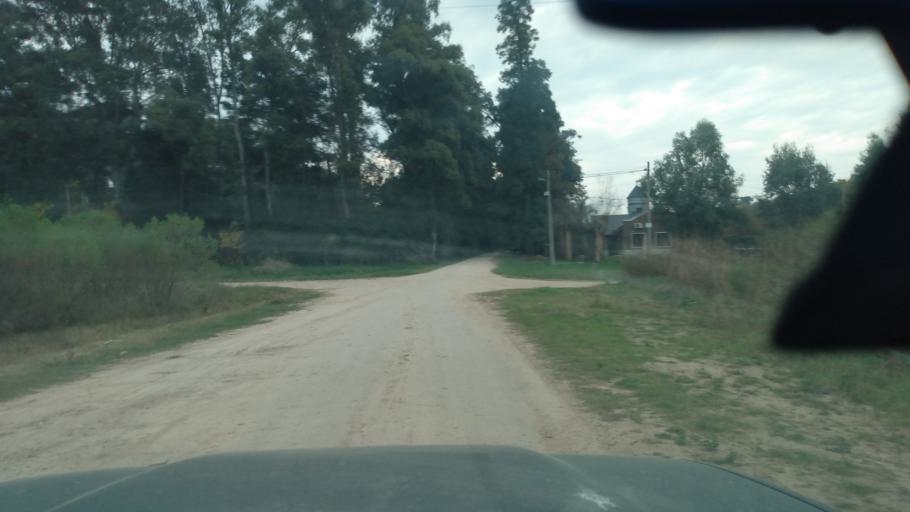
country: AR
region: Buenos Aires
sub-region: Partido de Lujan
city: Lujan
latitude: -34.5589
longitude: -59.1570
